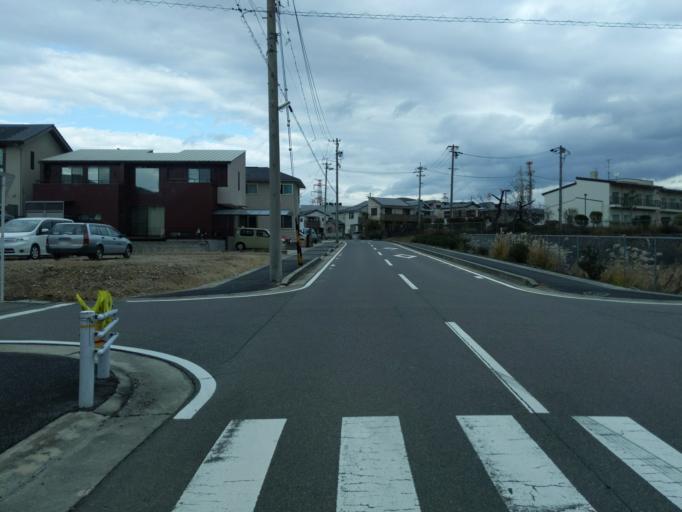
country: JP
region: Aichi
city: Kasugai
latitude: 35.2594
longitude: 136.9919
